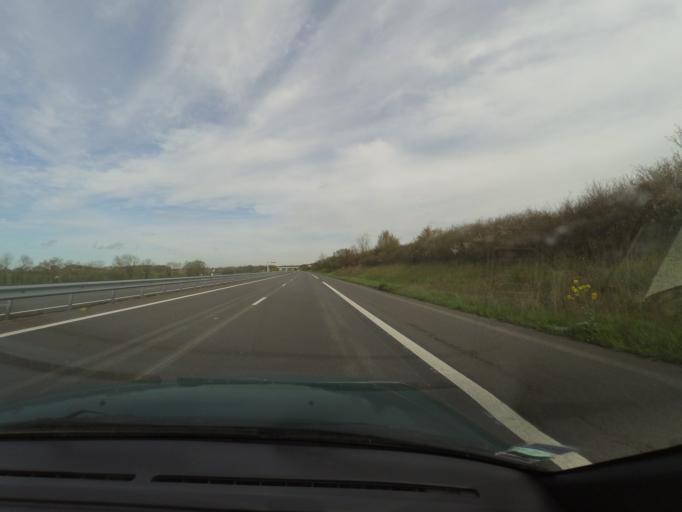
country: FR
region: Pays de la Loire
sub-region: Departement de la Loire-Atlantique
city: Aigrefeuille-sur-Maine
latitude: 47.0749
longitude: -1.4398
